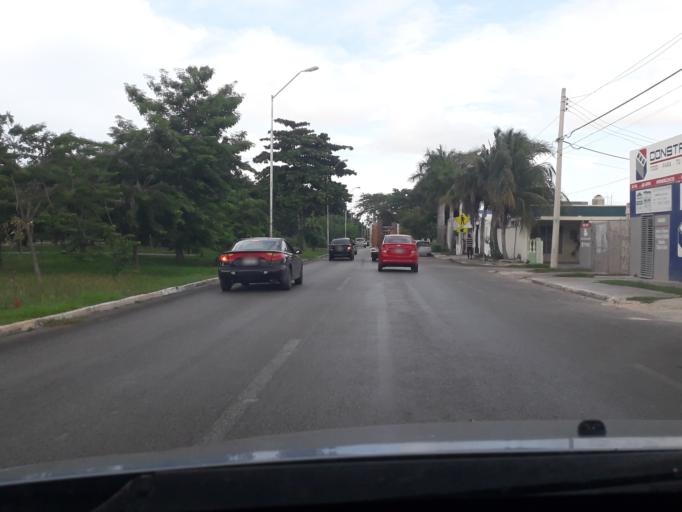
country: MX
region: Yucatan
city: Merida
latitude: 20.9815
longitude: -89.6633
